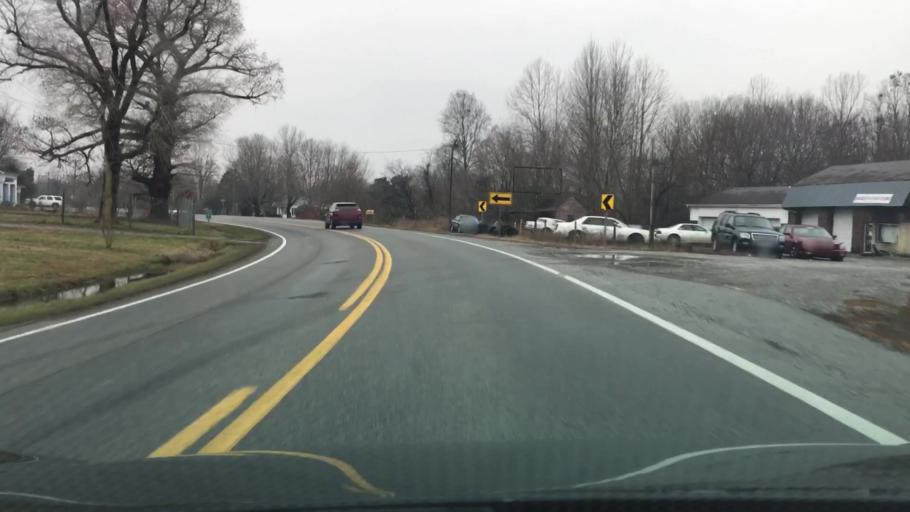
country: US
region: Kentucky
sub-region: Marshall County
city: Calvert City
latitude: 36.9735
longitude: -88.3999
